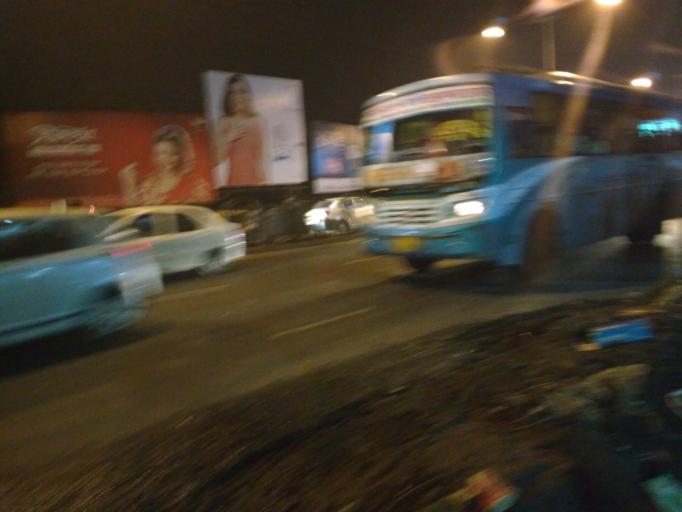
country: IN
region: West Bengal
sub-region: North 24 Parganas
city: Baranagar
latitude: 22.6314
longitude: 88.3786
